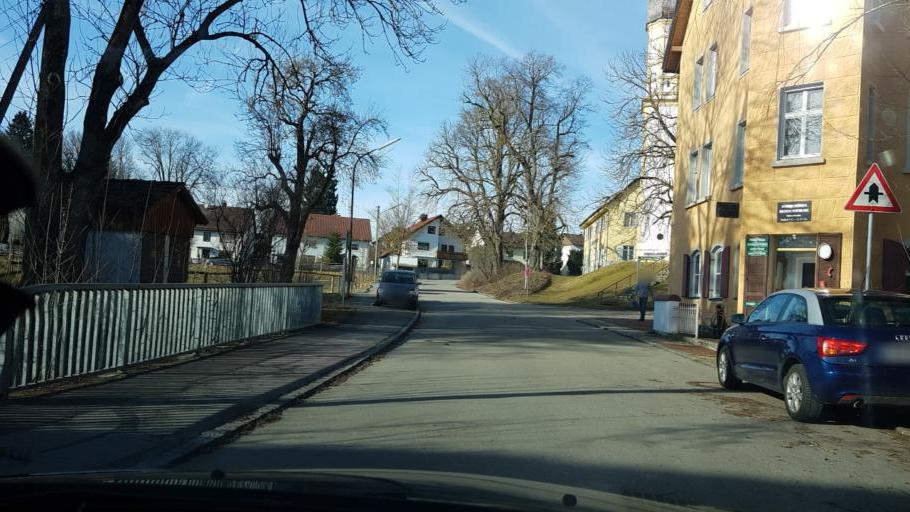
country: DE
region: Bavaria
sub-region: Upper Bavaria
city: Oberschweinbach
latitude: 48.2180
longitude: 11.1737
